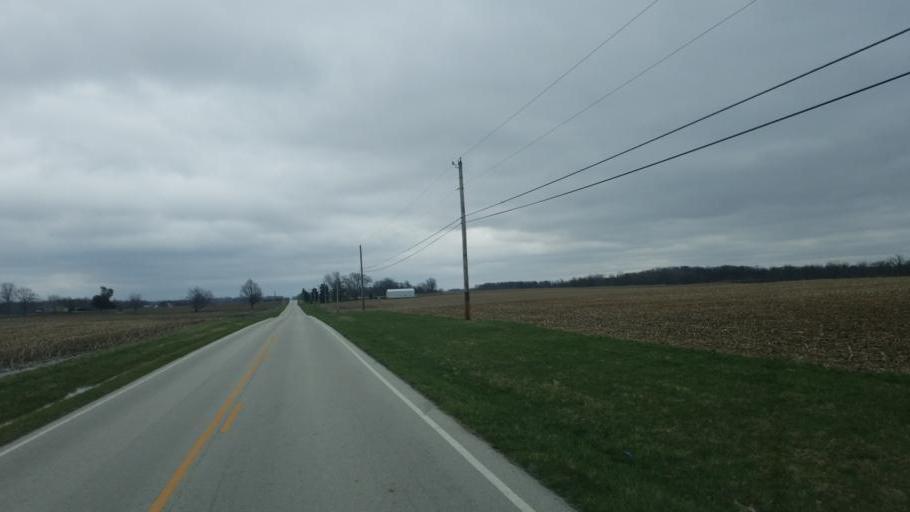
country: US
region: Ohio
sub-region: Wyandot County
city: Upper Sandusky
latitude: 40.8258
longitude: -83.2191
